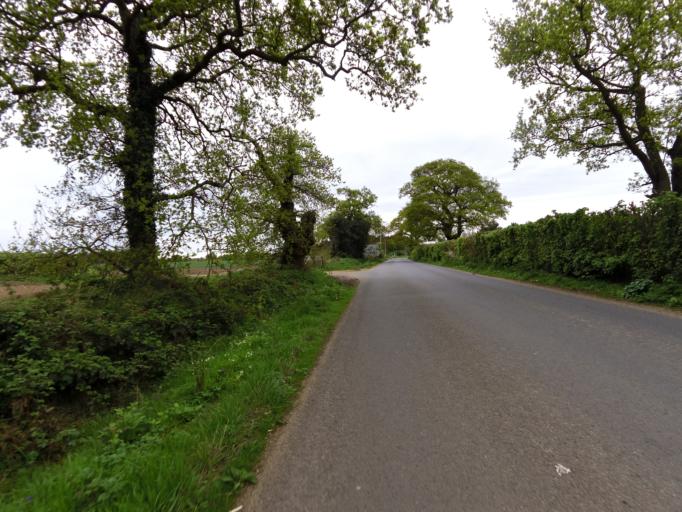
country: GB
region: England
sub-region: Suffolk
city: Kesgrave
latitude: 52.0238
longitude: 1.2098
